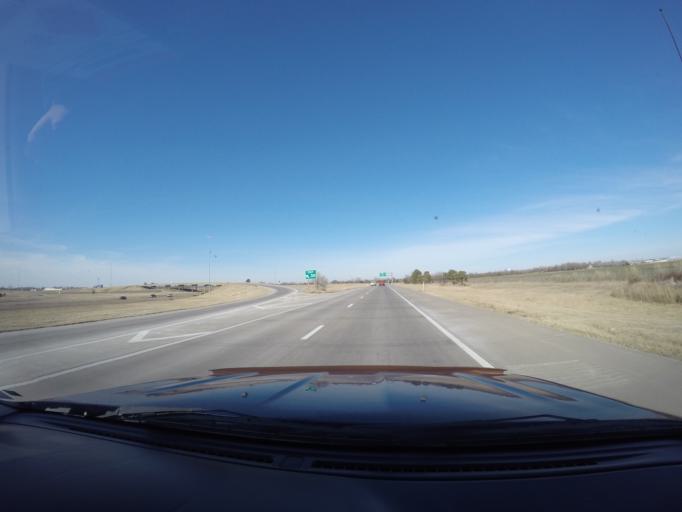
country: US
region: Kansas
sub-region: Harvey County
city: Newton
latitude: 38.0244
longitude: -97.3278
